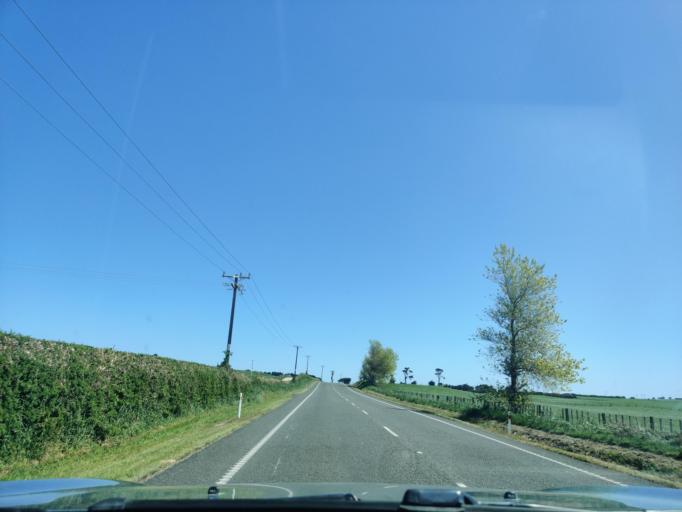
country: NZ
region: Taranaki
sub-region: South Taranaki District
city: Patea
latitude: -39.7774
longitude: 174.6863
